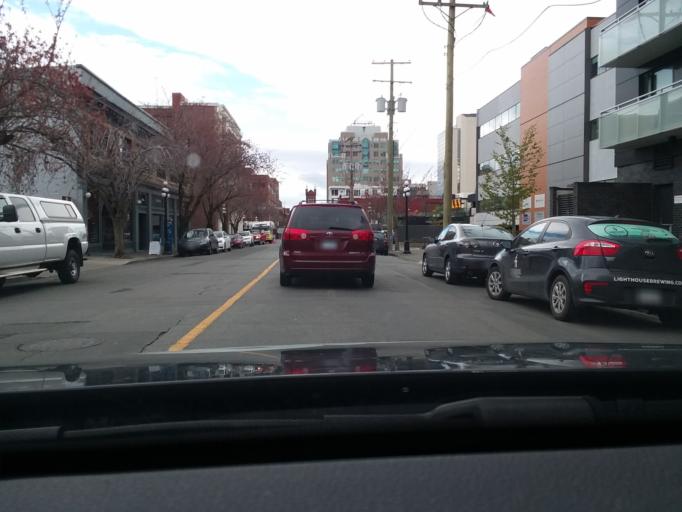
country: CA
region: British Columbia
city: Victoria
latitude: 48.4234
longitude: -123.3610
